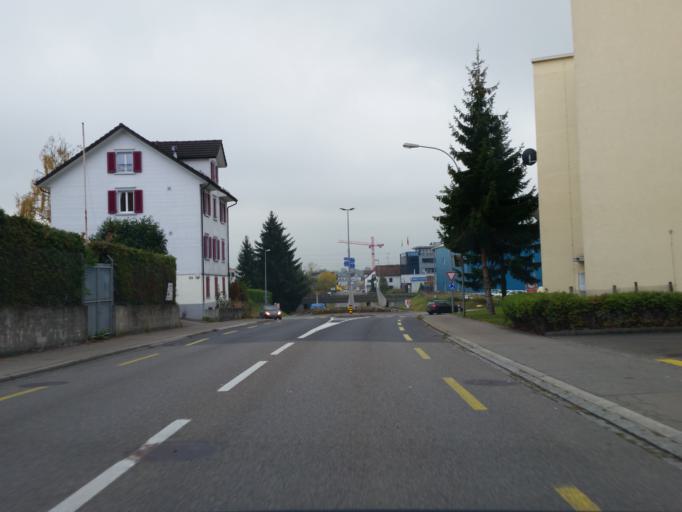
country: CH
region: Thurgau
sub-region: Arbon District
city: Salmsach
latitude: 47.5595
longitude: 9.3688
